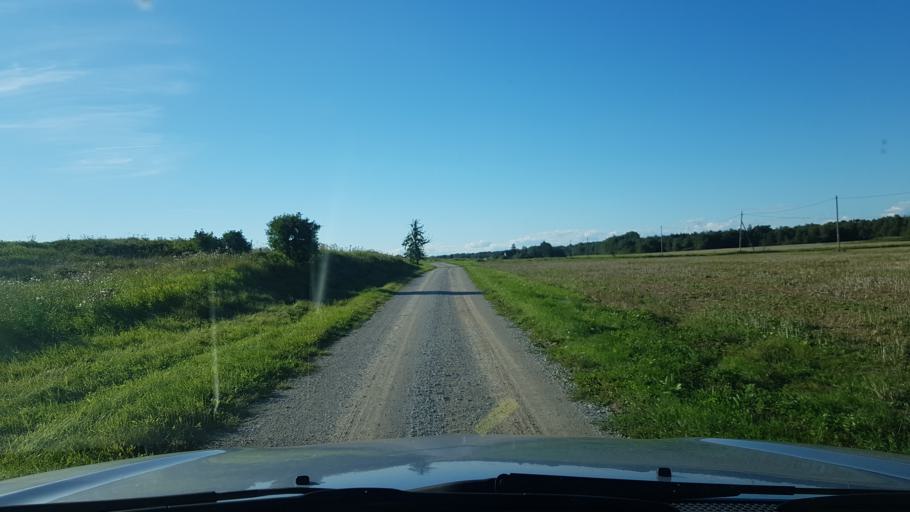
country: EE
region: Harju
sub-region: Rae vald
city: Jueri
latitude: 59.3843
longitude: 24.8818
